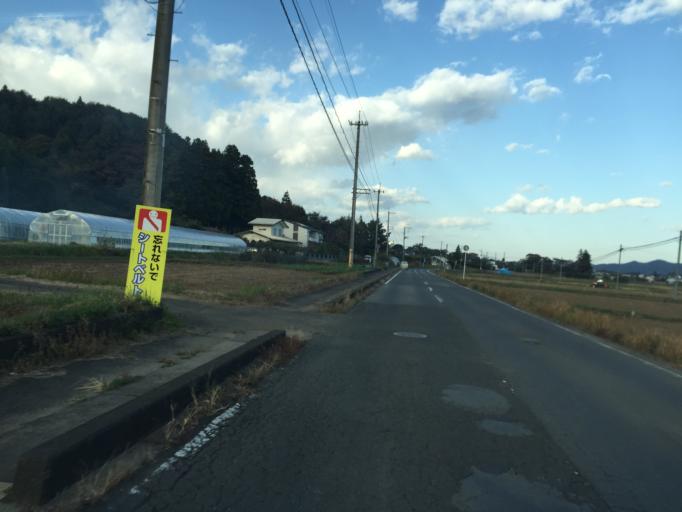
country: JP
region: Fukushima
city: Fukushima-shi
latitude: 37.7054
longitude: 140.4267
